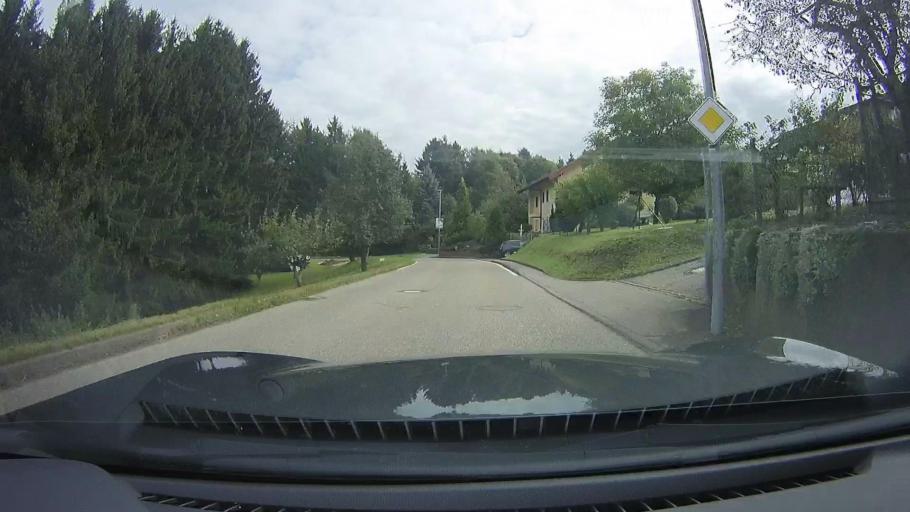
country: DE
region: Baden-Wuerttemberg
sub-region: Regierungsbezirk Stuttgart
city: Wustenrot
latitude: 49.0863
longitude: 9.4377
